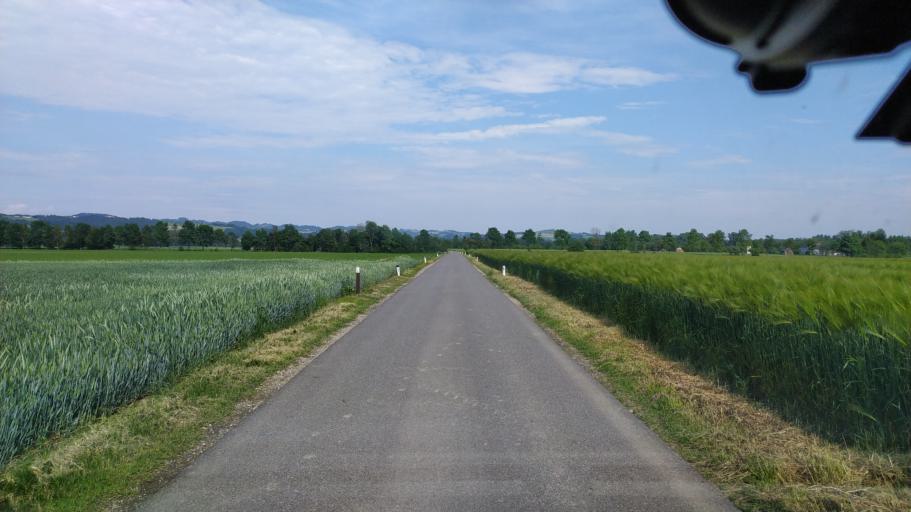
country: AT
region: Upper Austria
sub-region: Politischer Bezirk Perg
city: Bad Kreuzen
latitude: 48.1955
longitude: 14.7604
